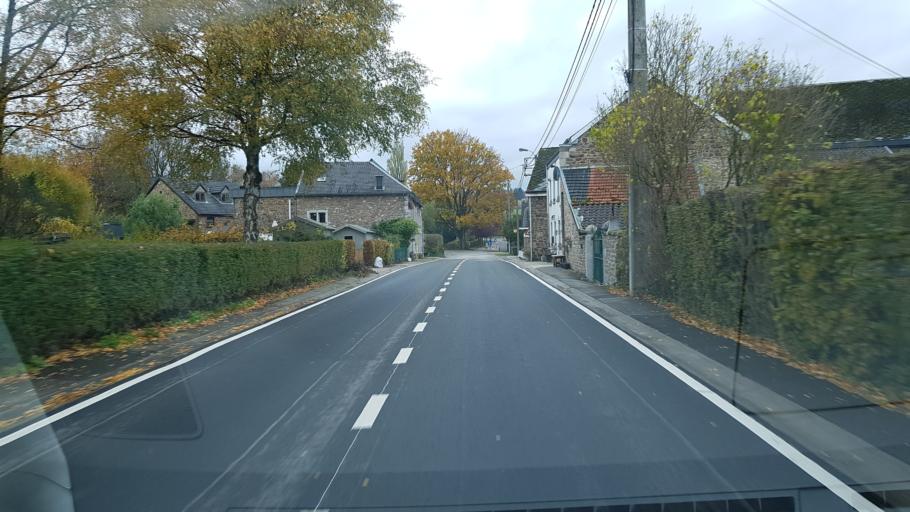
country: BE
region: Wallonia
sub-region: Province de Liege
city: Theux
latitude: 50.4915
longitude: 5.7927
